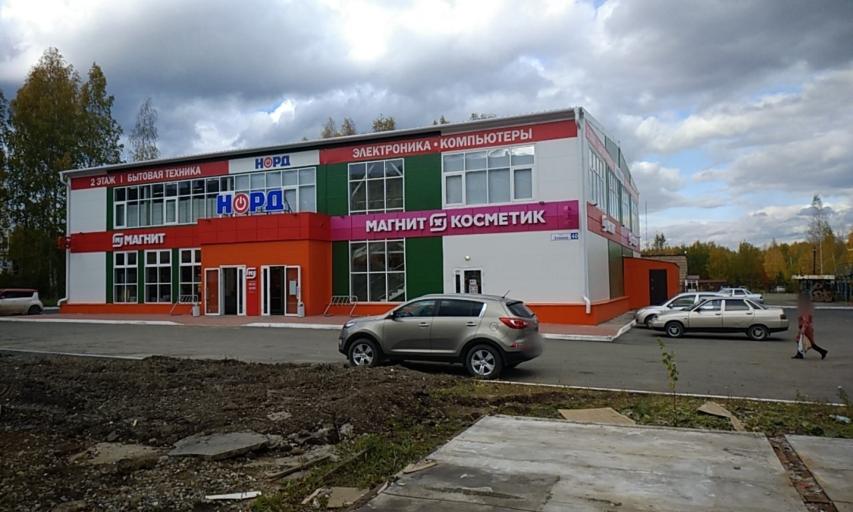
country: RU
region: Sverdlovsk
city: Krasnoural'sk
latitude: 58.3586
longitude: 60.0304
